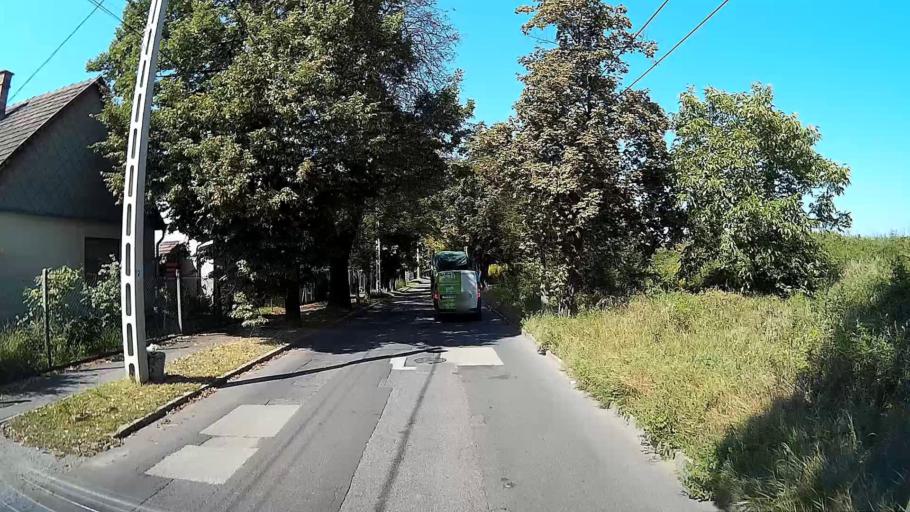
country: HU
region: Budapest
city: Budapest XVIII. keruelet
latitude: 47.4529
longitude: 19.1908
